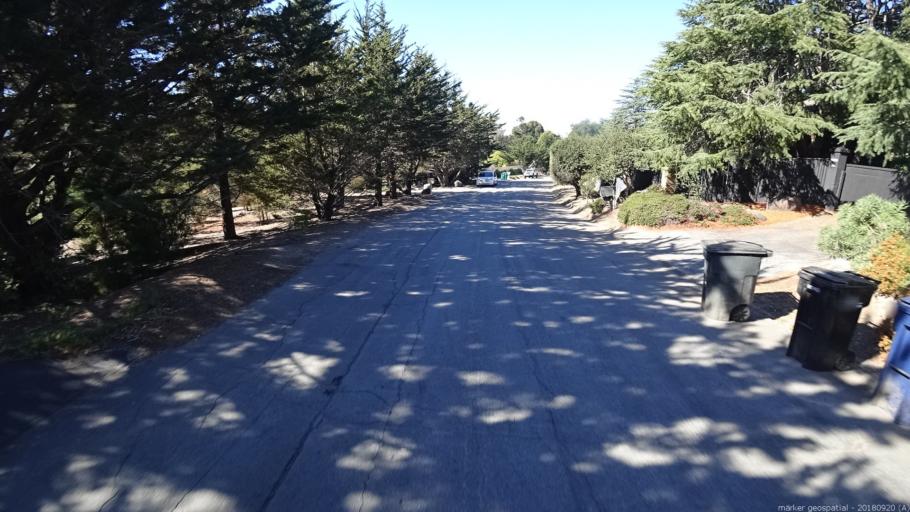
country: US
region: California
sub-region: Monterey County
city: Carmel-by-the-Sea
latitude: 36.5461
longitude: -121.8972
